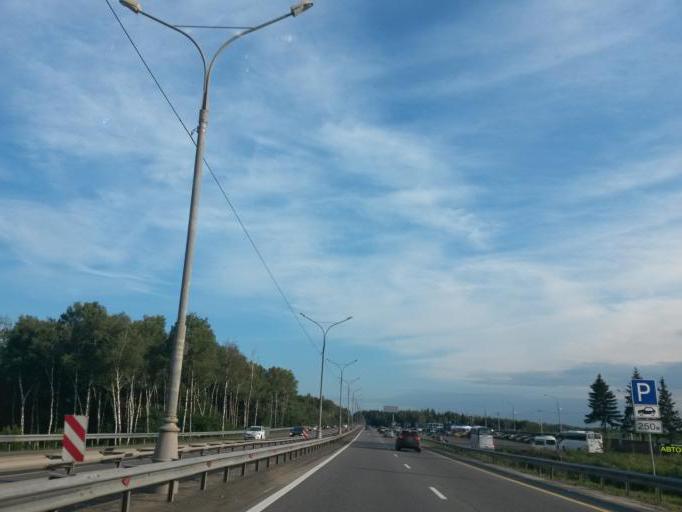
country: RU
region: Moskovskaya
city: Vostryakovo
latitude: 55.4686
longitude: 37.8535
